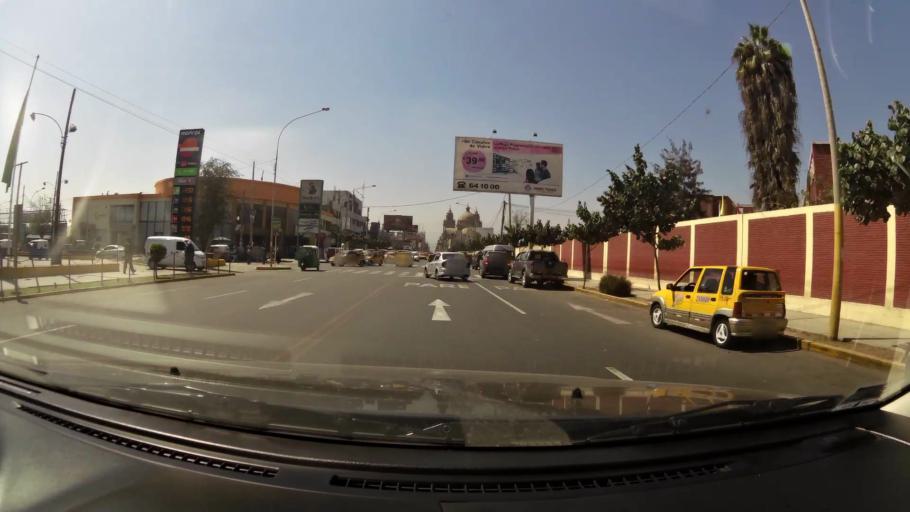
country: PE
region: Ica
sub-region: Provincia de Ica
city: Ica
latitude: -14.0648
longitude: -75.7338
